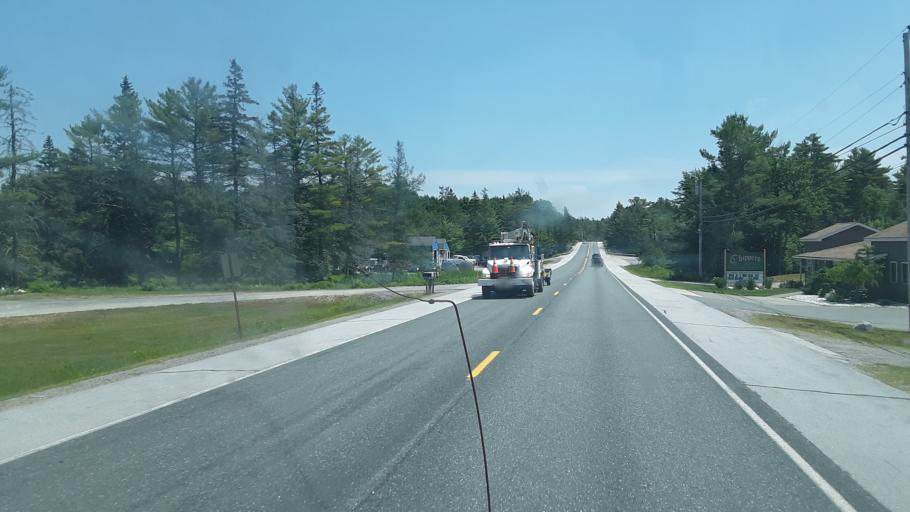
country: US
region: Maine
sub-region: Hancock County
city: Hancock
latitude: 44.5340
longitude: -68.2715
